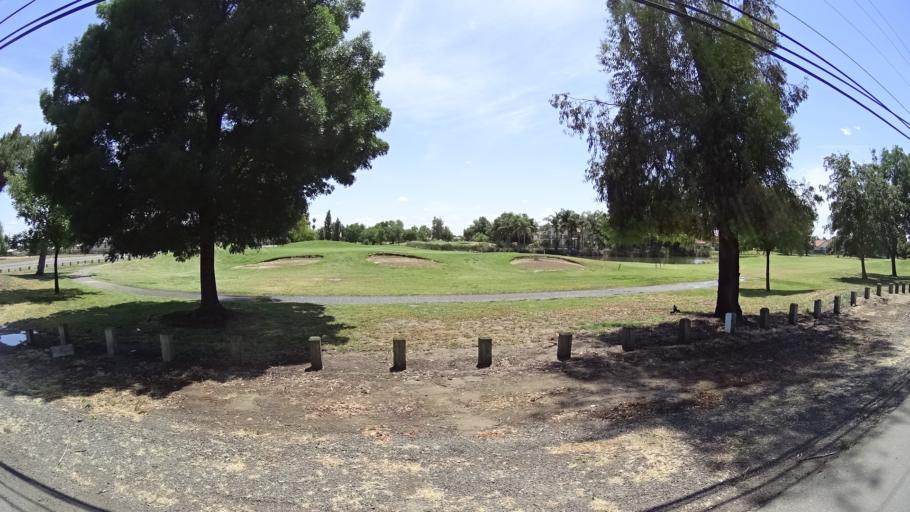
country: US
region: California
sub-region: Kings County
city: Lemoore
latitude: 36.2837
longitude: -119.7815
